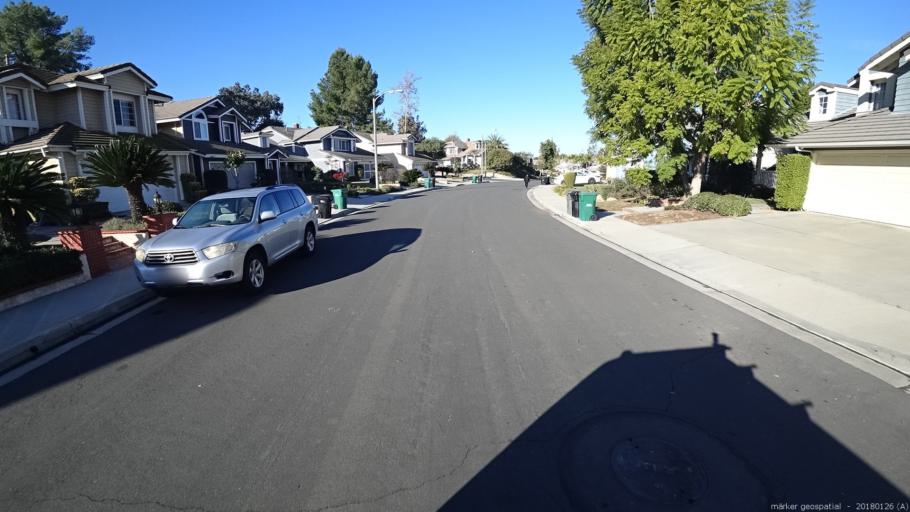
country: US
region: California
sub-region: Los Angeles County
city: Walnut
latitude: 33.9823
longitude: -117.8465
